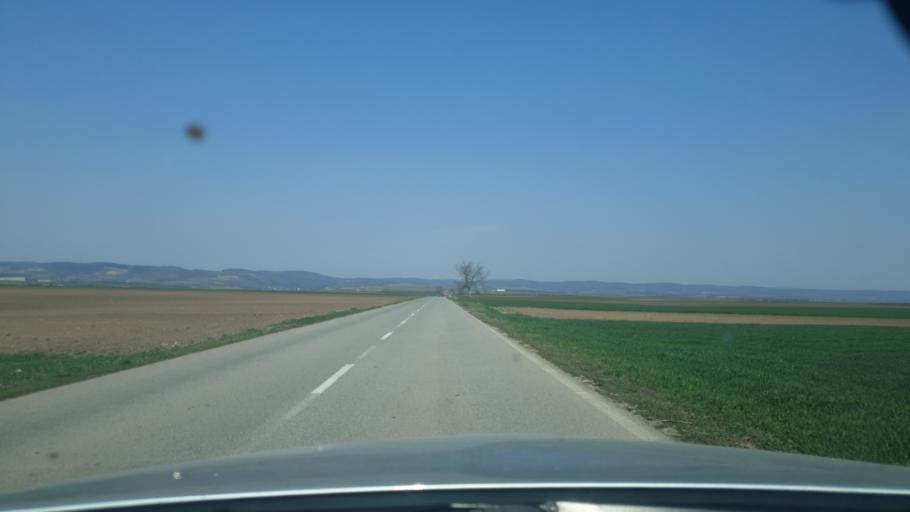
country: RS
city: Vrdnik
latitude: 45.0556
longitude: 19.7663
